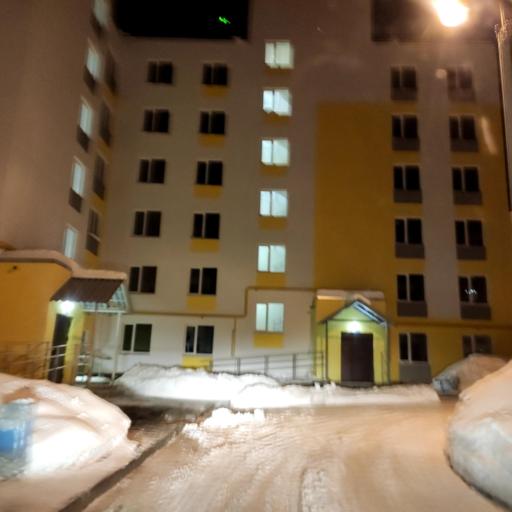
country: RU
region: Bashkortostan
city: Mikhaylovka
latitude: 54.7544
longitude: 55.7914
